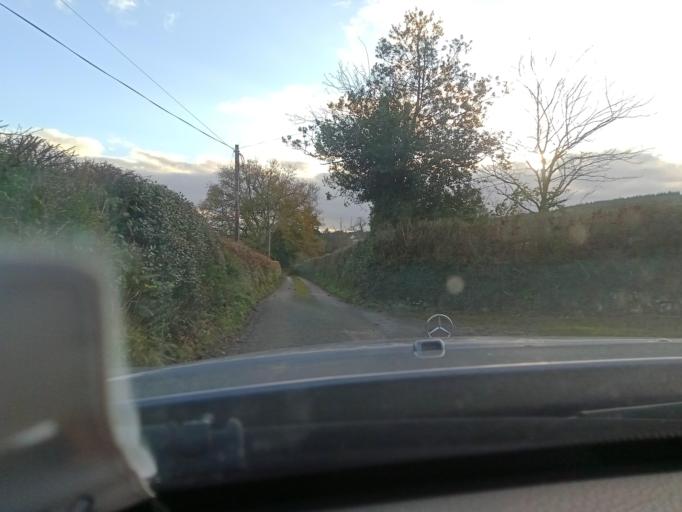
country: IE
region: Leinster
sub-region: Kilkenny
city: Graiguenamanagh
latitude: 52.5053
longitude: -6.9416
